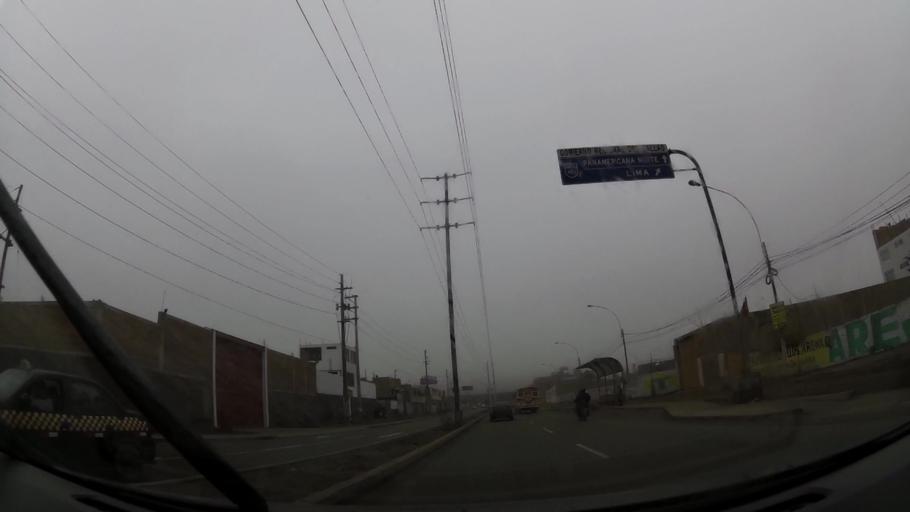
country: PE
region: Lima
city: Ventanilla
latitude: -11.8386
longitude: -77.1120
